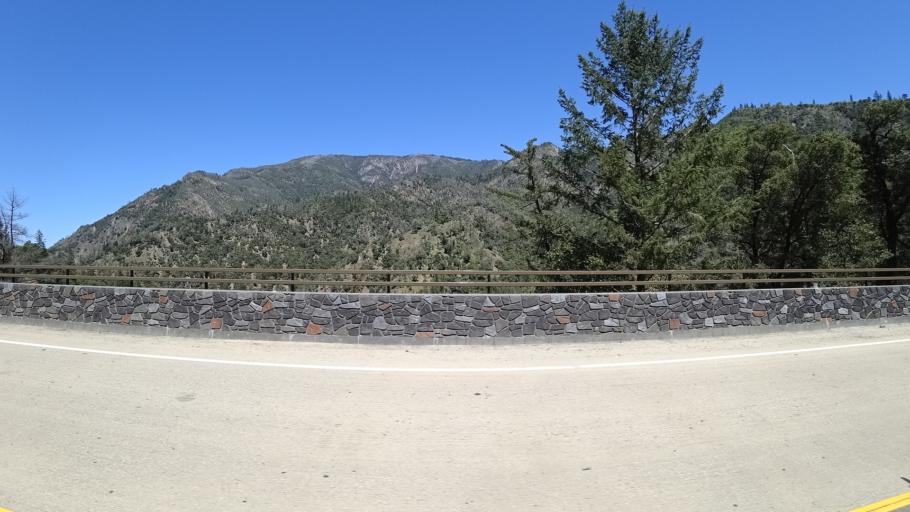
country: US
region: California
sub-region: Humboldt County
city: Willow Creek
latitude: 40.7973
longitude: -123.4615
